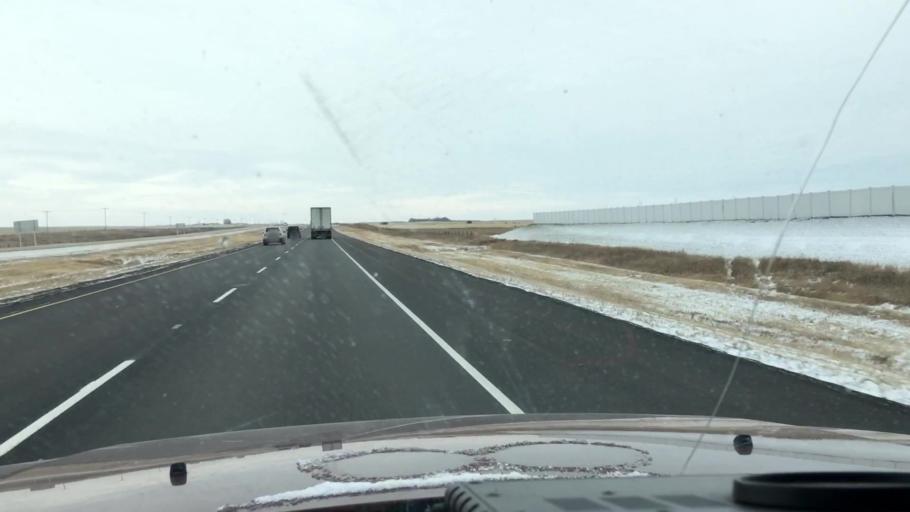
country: CA
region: Saskatchewan
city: Saskatoon
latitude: 51.8036
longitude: -106.4917
